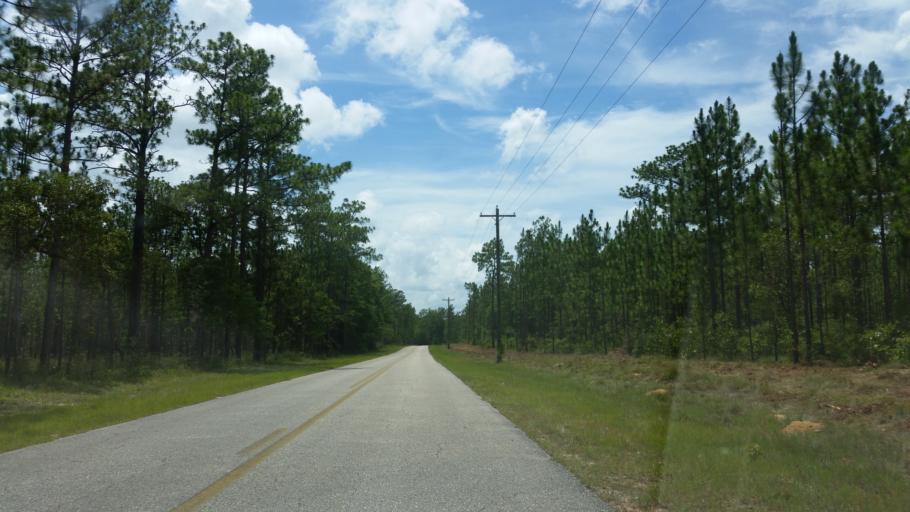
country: US
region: Florida
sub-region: Santa Rosa County
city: East Milton
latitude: 30.7360
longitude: -86.8221
